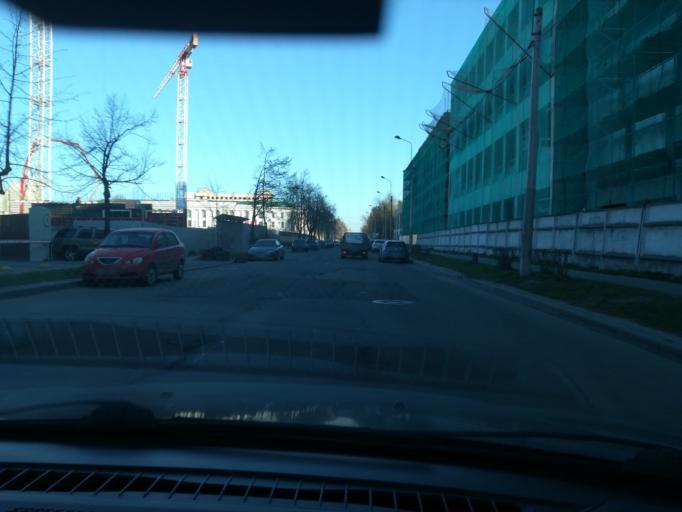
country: RU
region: St.-Petersburg
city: Vasyl'evsky Ostrov
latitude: 59.9380
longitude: 30.2540
